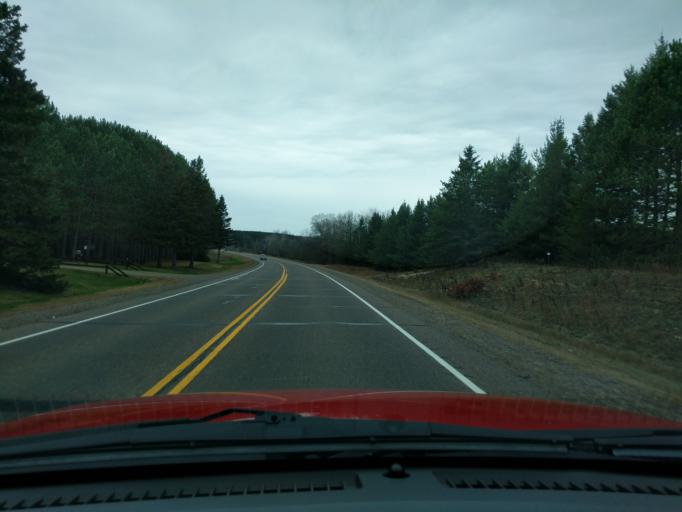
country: US
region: Wisconsin
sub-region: Washburn County
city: Spooner
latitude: 45.8240
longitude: -91.9443
